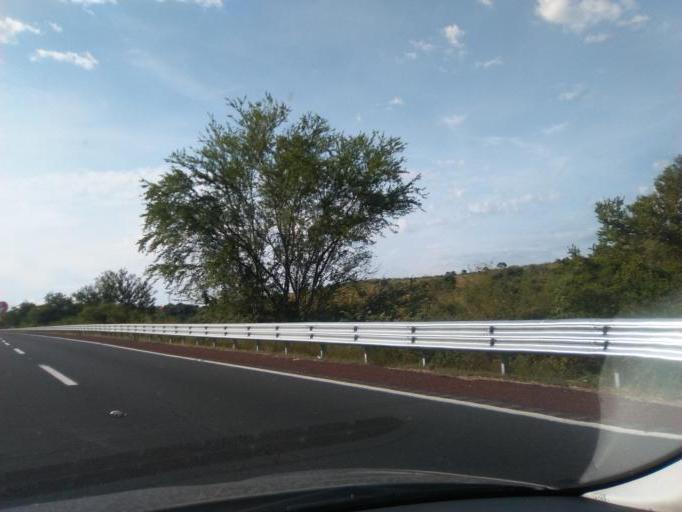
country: MX
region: Morelos
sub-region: Jojutla
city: Tehuixtla
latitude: 18.5777
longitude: -99.2403
